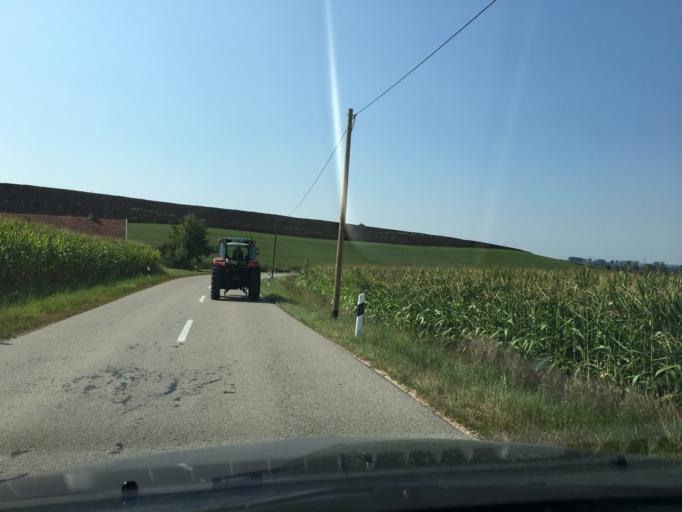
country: DE
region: Bavaria
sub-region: Upper Bavaria
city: Mettenheim
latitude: 48.2910
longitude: 12.4827
